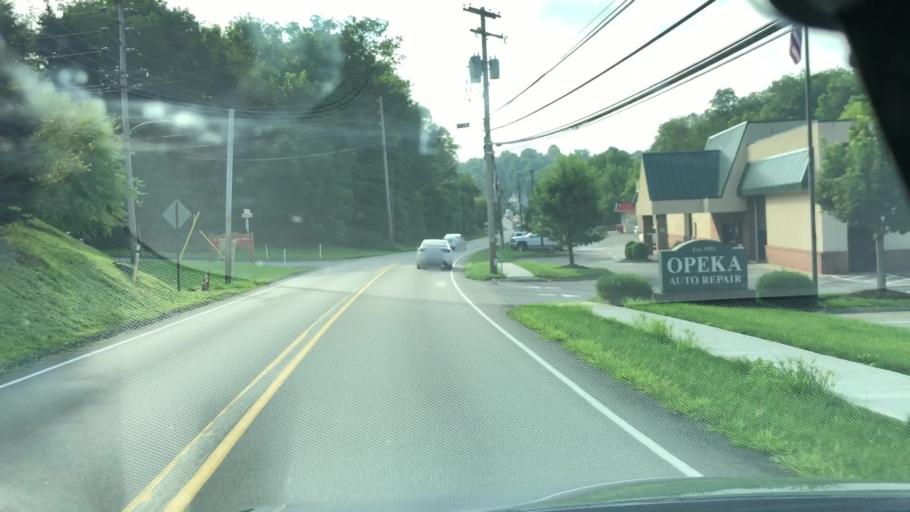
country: US
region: Pennsylvania
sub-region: Washington County
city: McMurray
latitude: 40.2813
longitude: -80.0882
